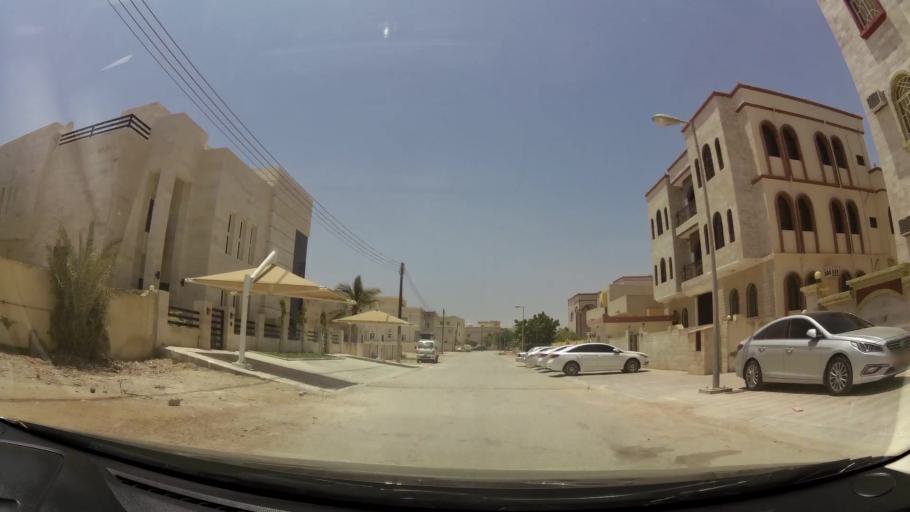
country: OM
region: Zufar
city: Salalah
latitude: 17.0837
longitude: 54.1496
